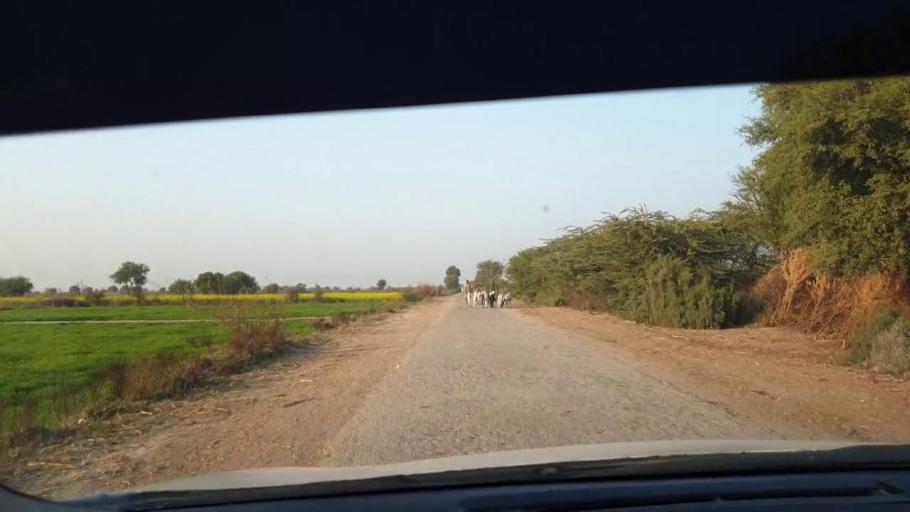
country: PK
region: Sindh
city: Berani
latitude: 25.8551
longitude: 68.8165
